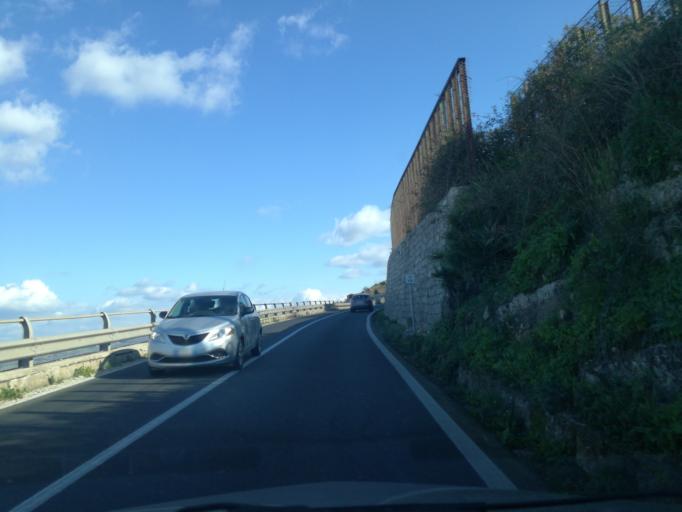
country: IT
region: Sicily
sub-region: Ragusa
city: Comiso
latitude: 36.9385
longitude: 14.6275
